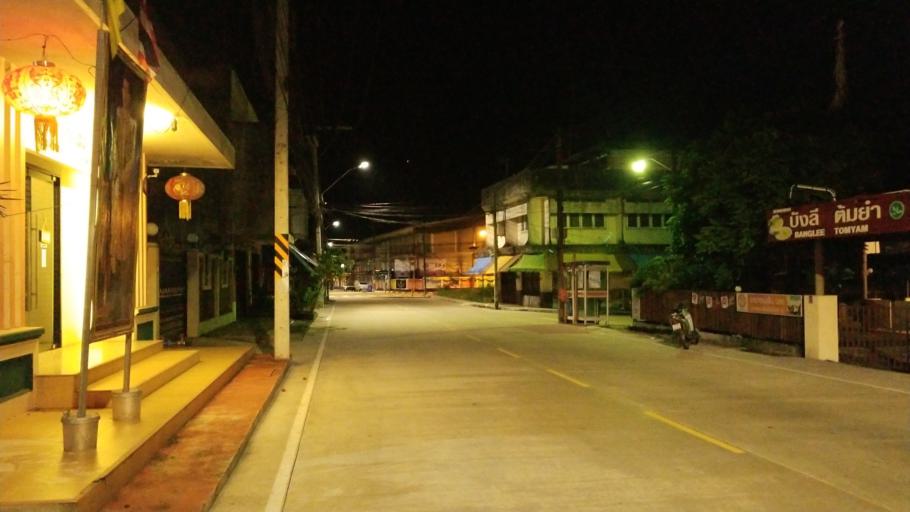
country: TH
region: Narathiwat
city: Su-ngai Kolok
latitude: 6.0218
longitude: 101.9618
